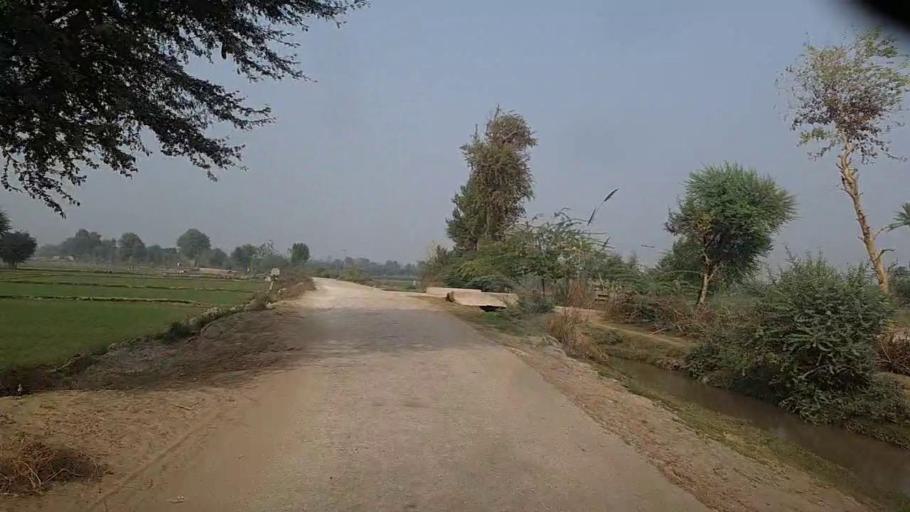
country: PK
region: Sindh
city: Bozdar
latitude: 27.0670
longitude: 68.6373
